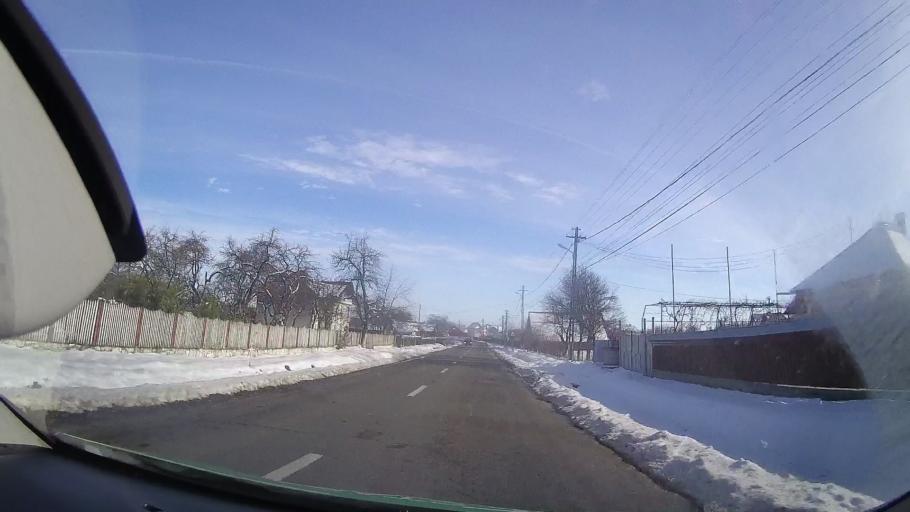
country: RO
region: Neamt
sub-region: Comuna Agapia
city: Agapia
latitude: 47.1726
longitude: 26.2905
